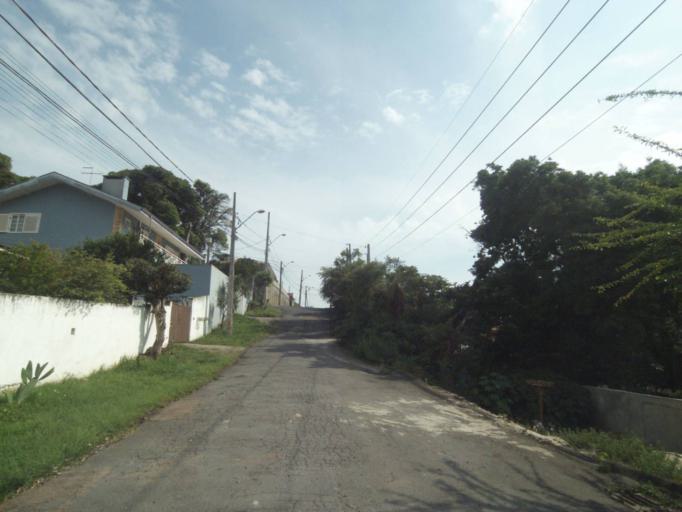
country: BR
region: Parana
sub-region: Curitiba
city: Curitiba
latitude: -25.4079
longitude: -49.3016
